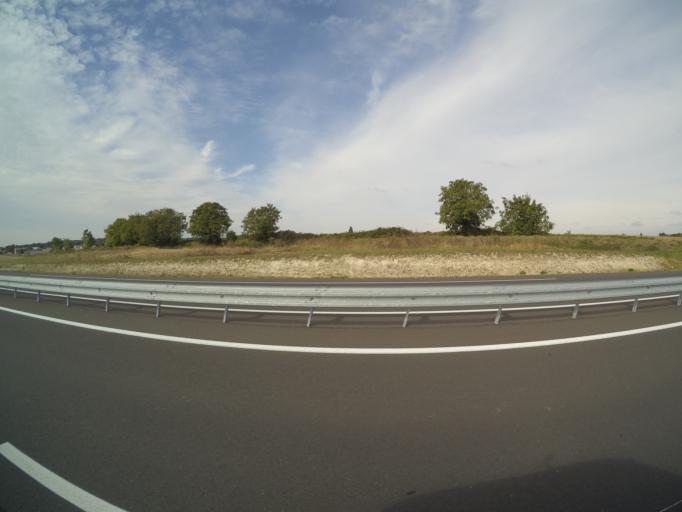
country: FR
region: Pays de la Loire
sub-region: Departement de Maine-et-Loire
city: Vaudelnay
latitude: 47.2102
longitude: -0.1859
